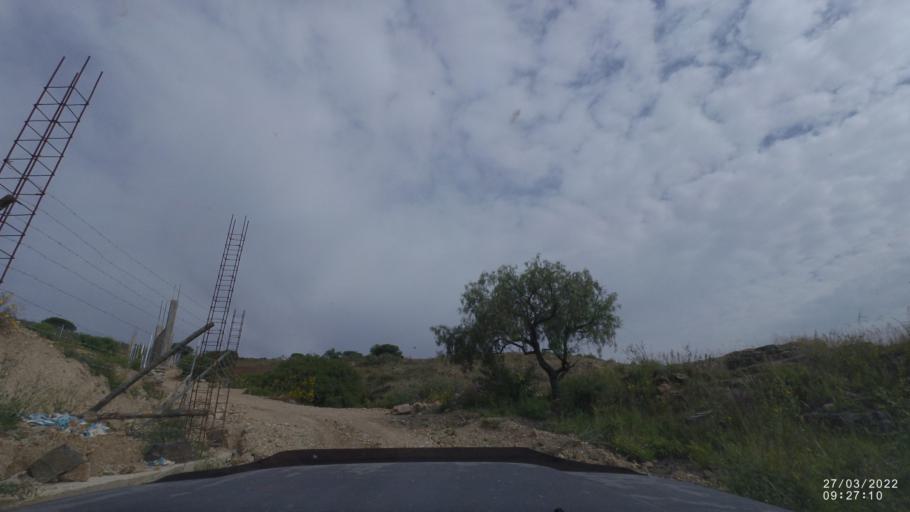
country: BO
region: Cochabamba
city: Cliza
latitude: -17.7296
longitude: -65.8756
